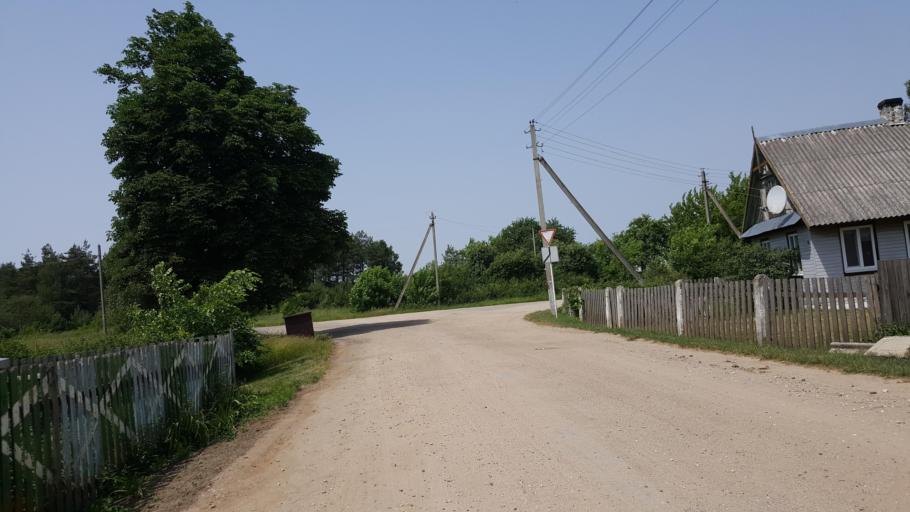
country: BY
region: Brest
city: Kamyanyets
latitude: 52.4806
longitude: 23.8773
